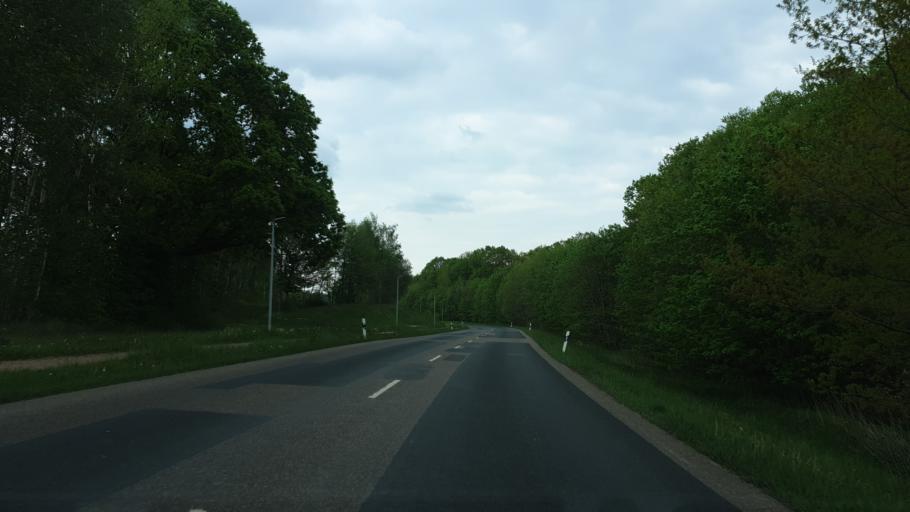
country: DE
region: Saxony
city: Neukirchen
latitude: 50.7683
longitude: 12.8705
